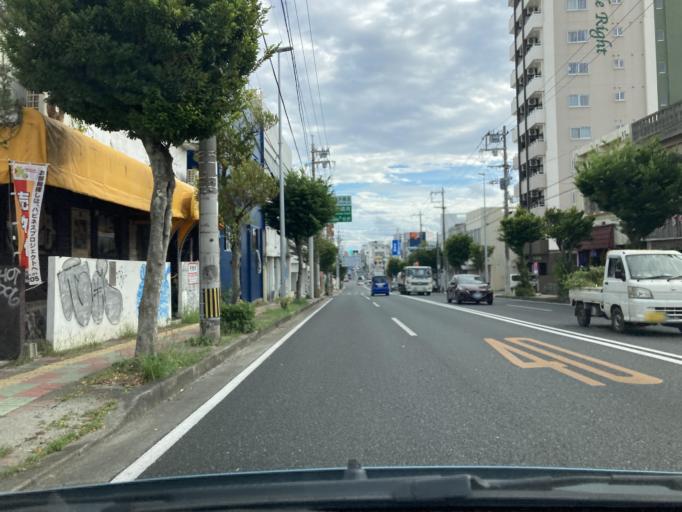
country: JP
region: Okinawa
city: Okinawa
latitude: 26.3415
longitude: 127.8143
